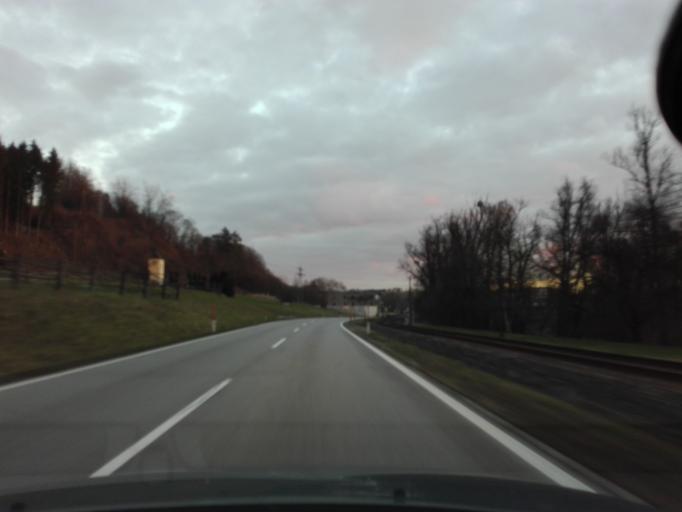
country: AT
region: Upper Austria
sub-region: Politischer Bezirk Perg
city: Bad Kreuzen
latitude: 48.1948
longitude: 14.8159
